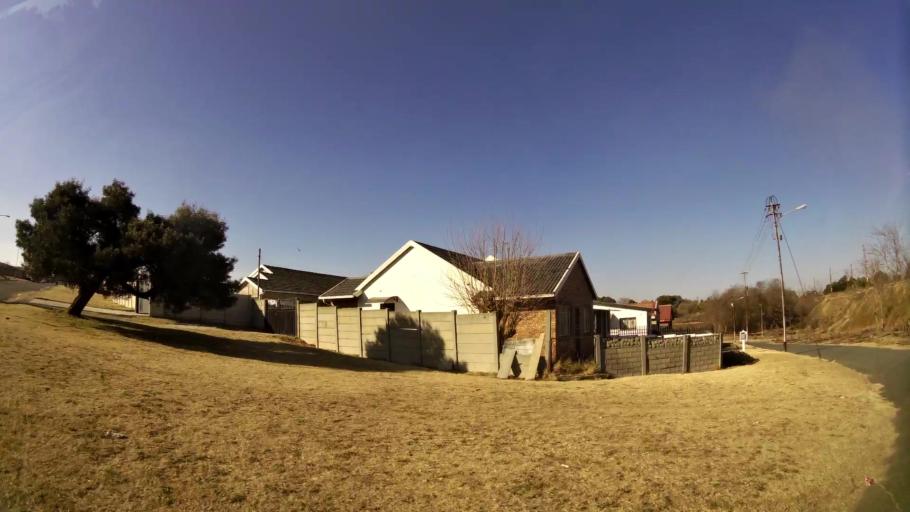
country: ZA
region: Gauteng
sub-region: City of Johannesburg Metropolitan Municipality
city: Johannesburg
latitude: -26.2152
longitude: 27.9714
